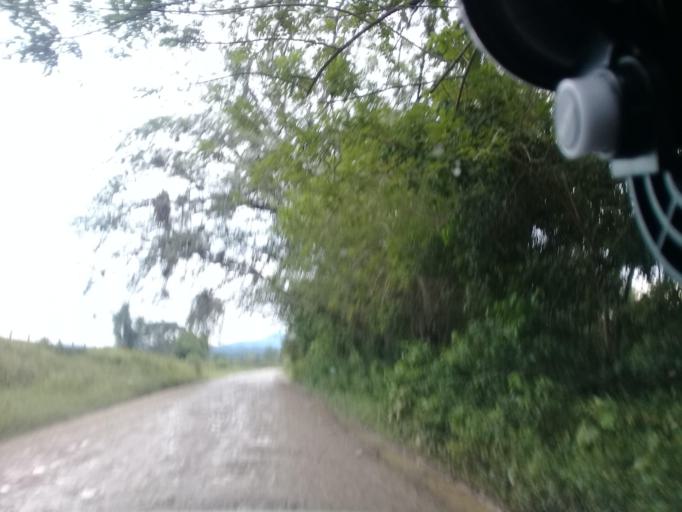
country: MX
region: Hidalgo
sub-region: Huejutla de Reyes
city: Chalahuiyapa
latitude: 21.1602
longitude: -98.3664
